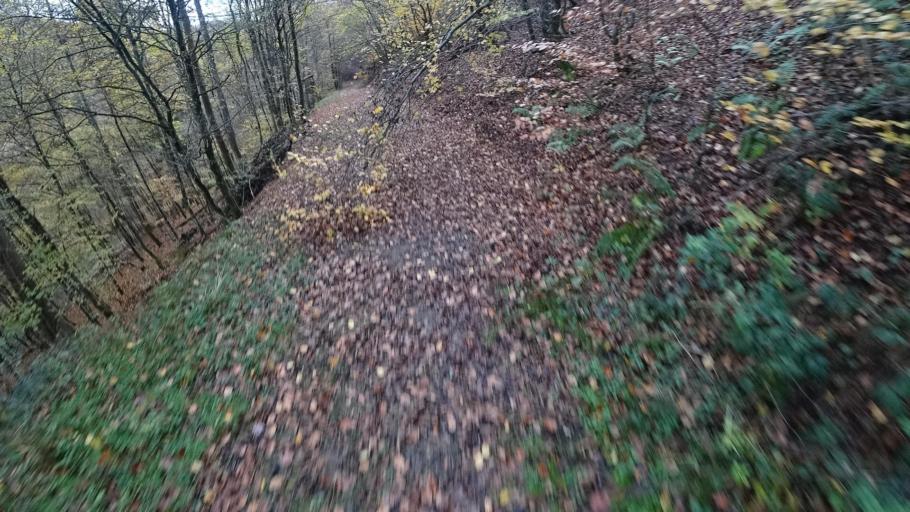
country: DE
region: Rheinland-Pfalz
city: Lind
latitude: 50.4887
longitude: 6.9174
